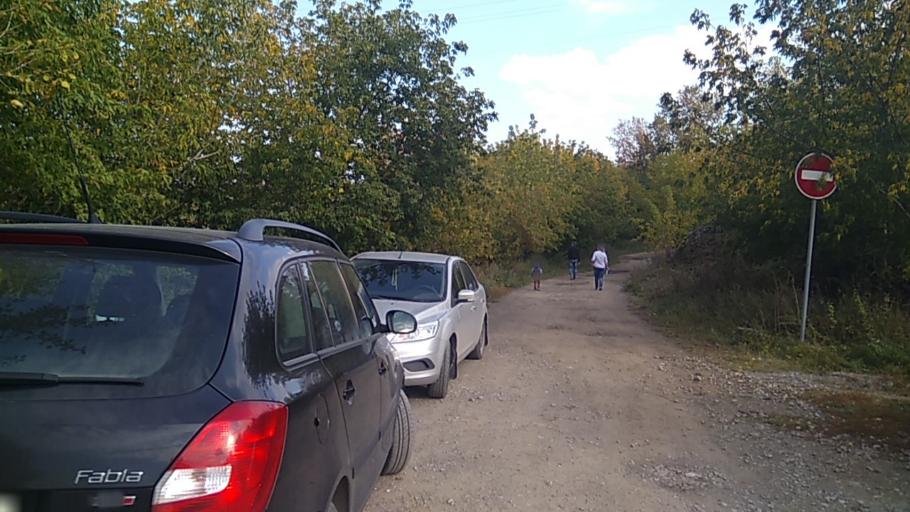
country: RU
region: Sverdlovsk
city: Pokrovskoye
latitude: 56.4357
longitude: 61.5920
